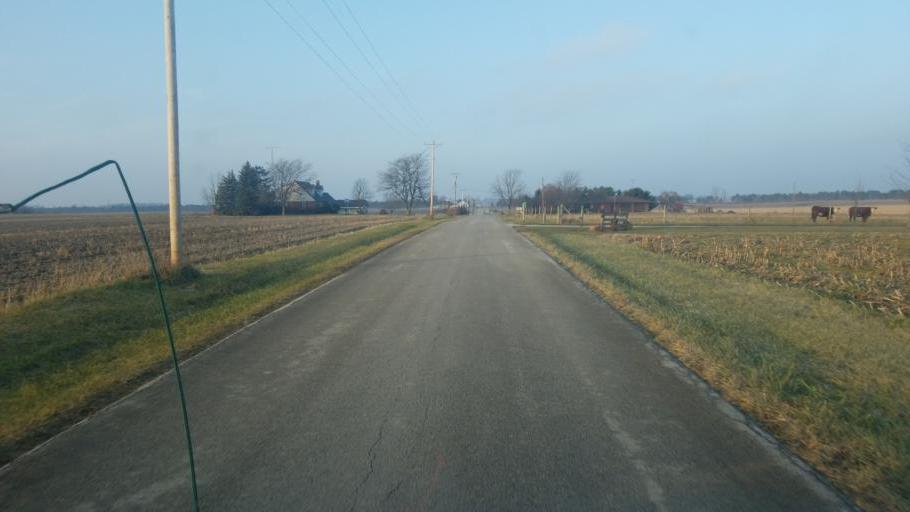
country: US
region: Ohio
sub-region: Wyandot County
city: Carey
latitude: 40.9433
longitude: -83.4291
